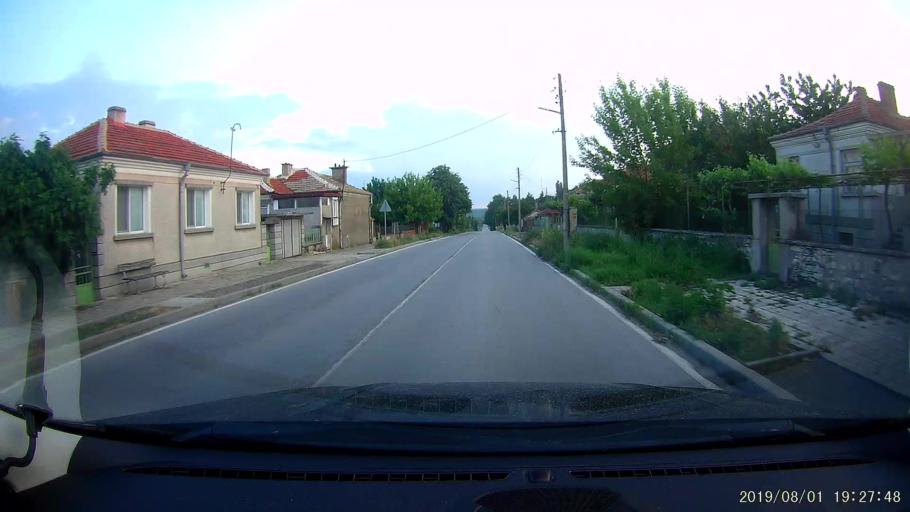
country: BG
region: Burgas
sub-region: Obshtina Sungurlare
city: Sungurlare
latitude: 42.8491
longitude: 26.9279
